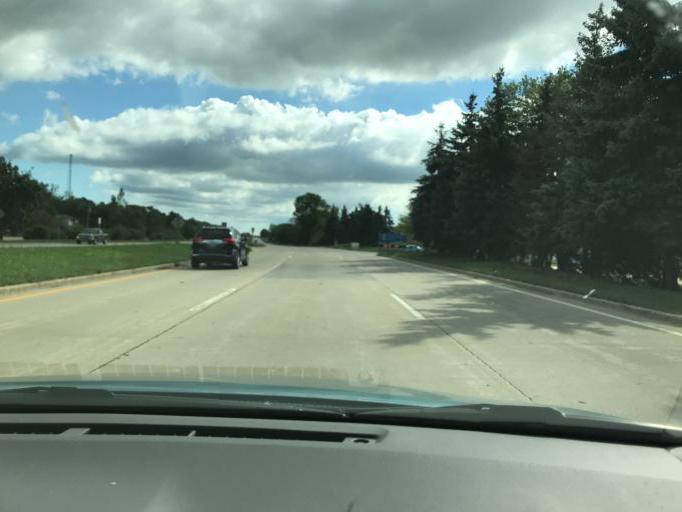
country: US
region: Wisconsin
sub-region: Kenosha County
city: Pleasant Prairie
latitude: 42.5511
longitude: -87.8923
